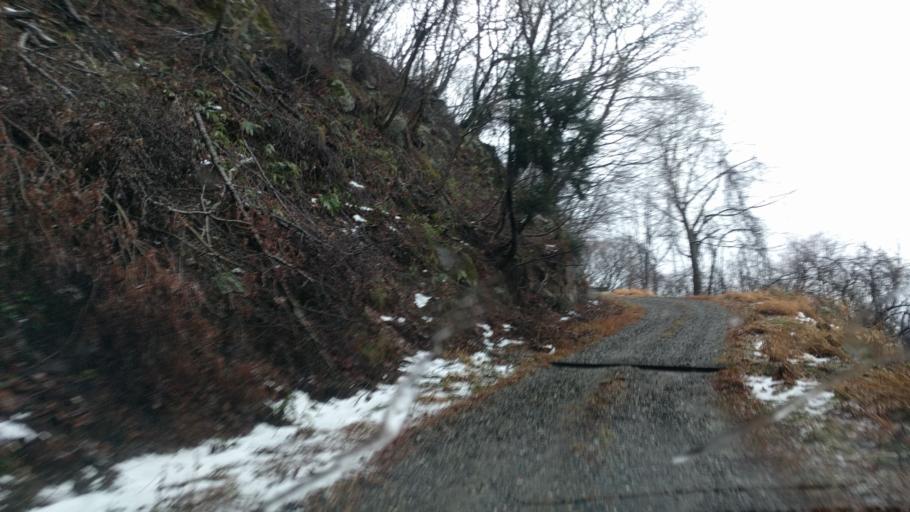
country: JP
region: Fukushima
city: Inawashiro
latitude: 37.5765
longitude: 139.9851
